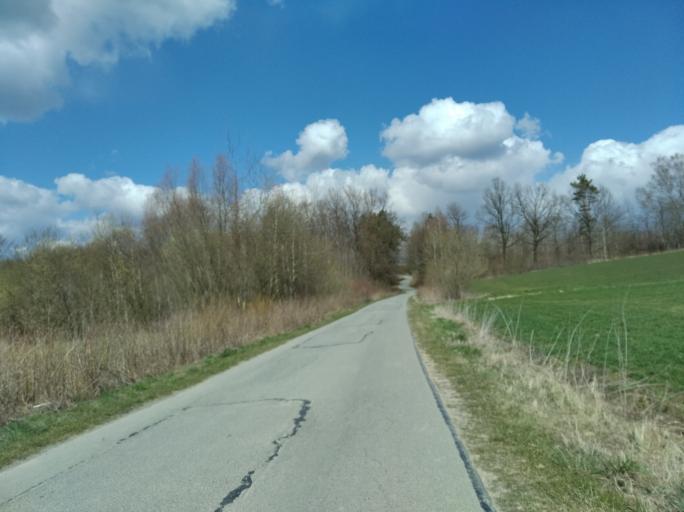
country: PL
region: Subcarpathian Voivodeship
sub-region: Powiat strzyzowski
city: Wisniowa
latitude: 49.9269
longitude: 21.7036
